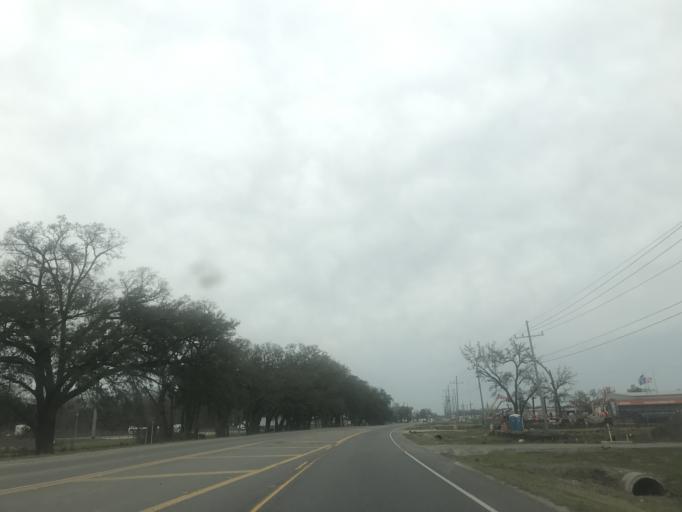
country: US
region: Louisiana
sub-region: Ascension Parish
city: Gonzales
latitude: 30.2117
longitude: -90.9974
